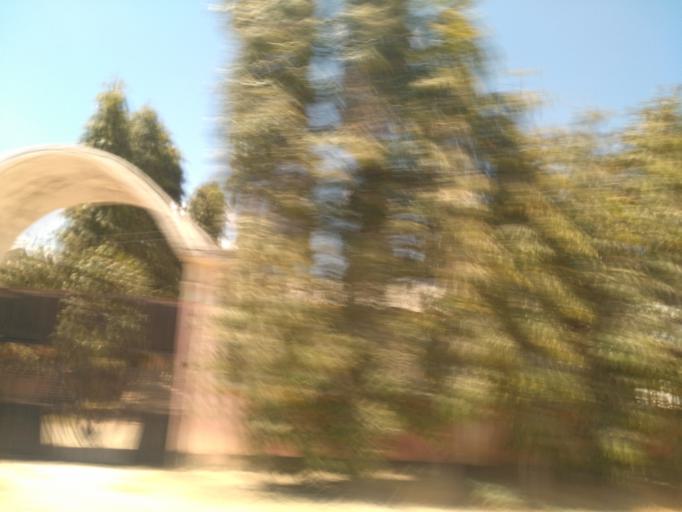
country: TZ
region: Dodoma
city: Kisasa
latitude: -6.1650
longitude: 35.7669
